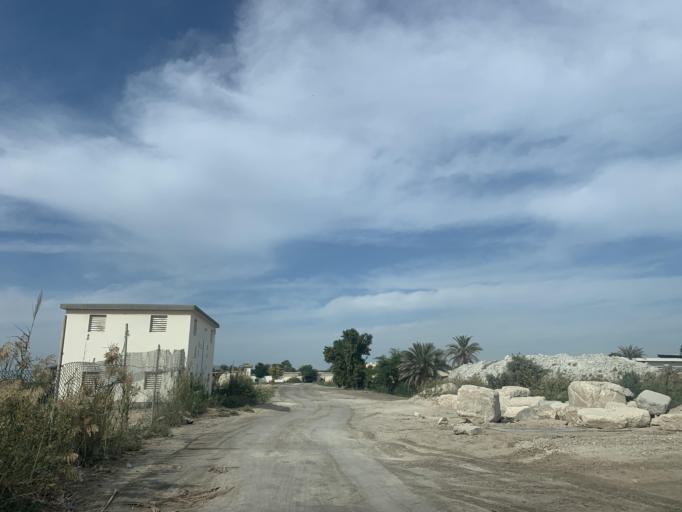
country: BH
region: Central Governorate
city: Madinat Hamad
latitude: 26.1177
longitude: 50.4703
